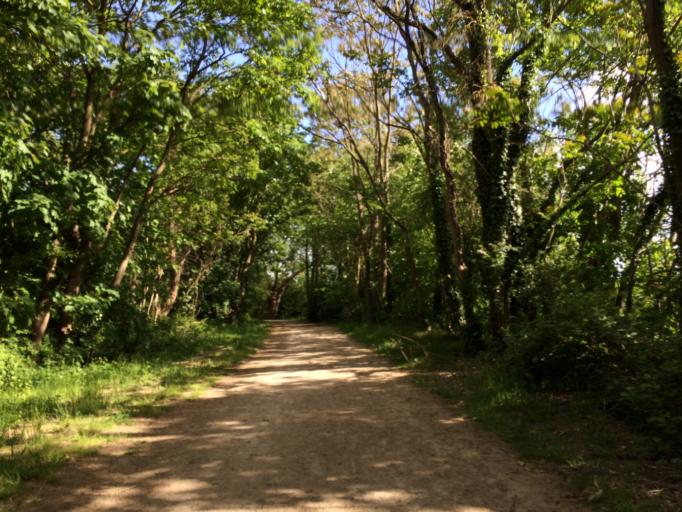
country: FR
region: Ile-de-France
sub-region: Departement de l'Essonne
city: Juvisy-sur-Orge
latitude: 48.6796
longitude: 2.3879
